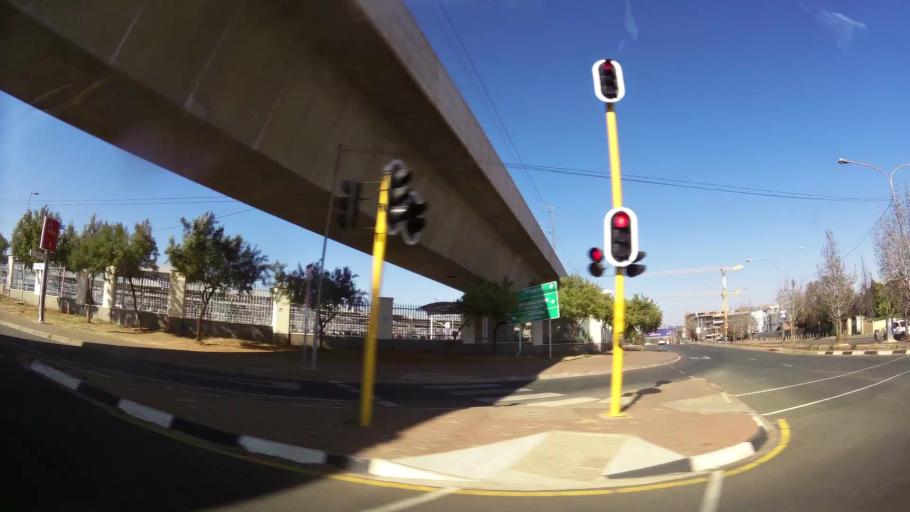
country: ZA
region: Gauteng
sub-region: City of Tshwane Metropolitan Municipality
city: Centurion
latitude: -25.8504
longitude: 28.1884
